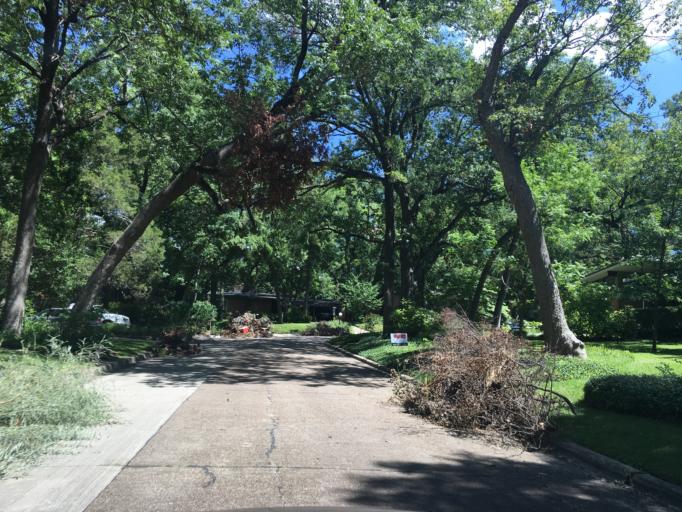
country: US
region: Texas
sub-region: Dallas County
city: Garland
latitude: 32.8448
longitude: -96.6996
